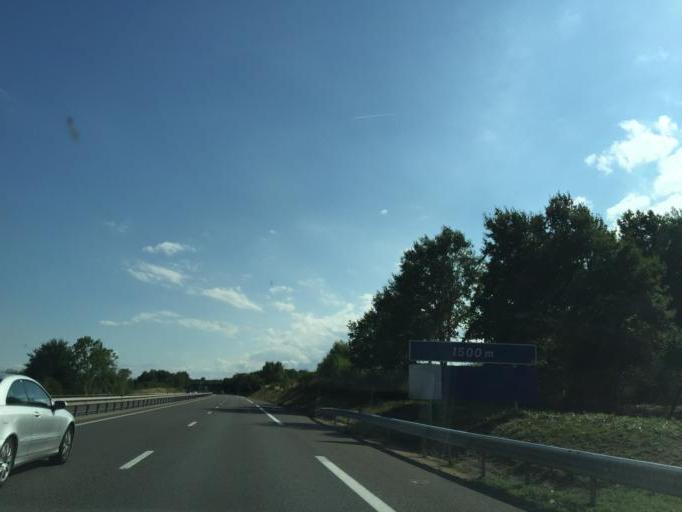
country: FR
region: Rhone-Alpes
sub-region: Departement de la Loire
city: Feurs
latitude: 45.7023
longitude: 4.1619
